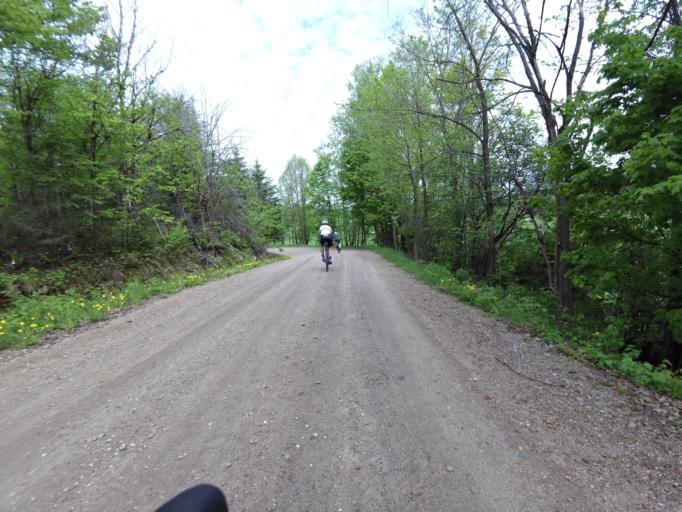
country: CA
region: Quebec
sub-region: Outaouais
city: Wakefield
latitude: 45.7718
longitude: -75.9237
